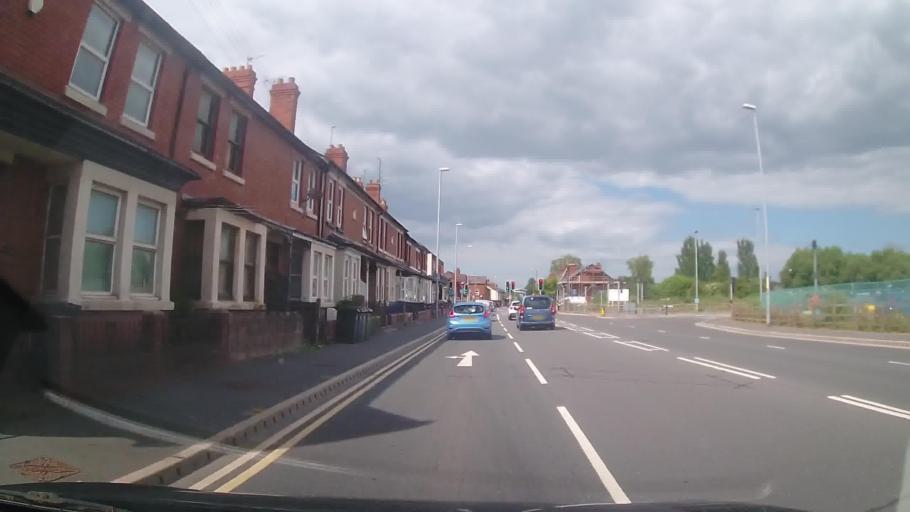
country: GB
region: England
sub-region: Herefordshire
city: Hereford
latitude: 52.0612
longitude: -2.7185
